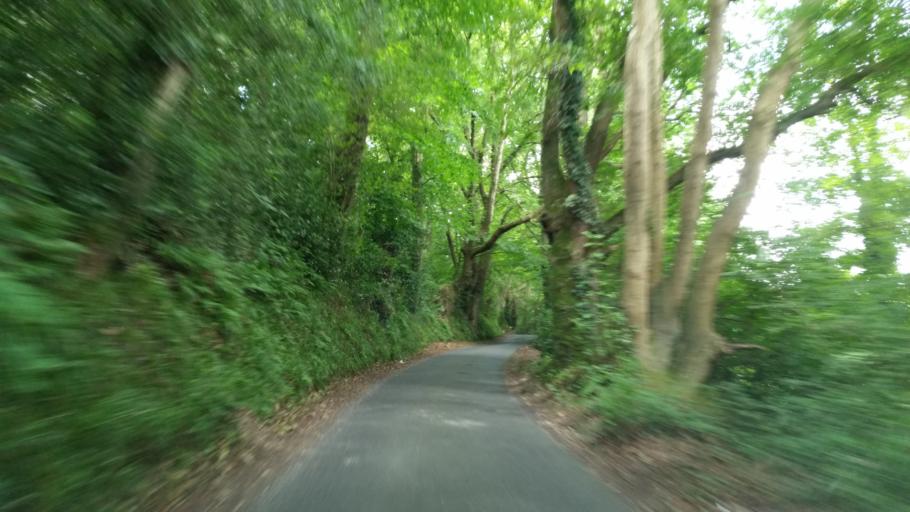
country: FR
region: Lower Normandy
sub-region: Departement du Calvados
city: Honfleur
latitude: 49.4104
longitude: 0.2311
